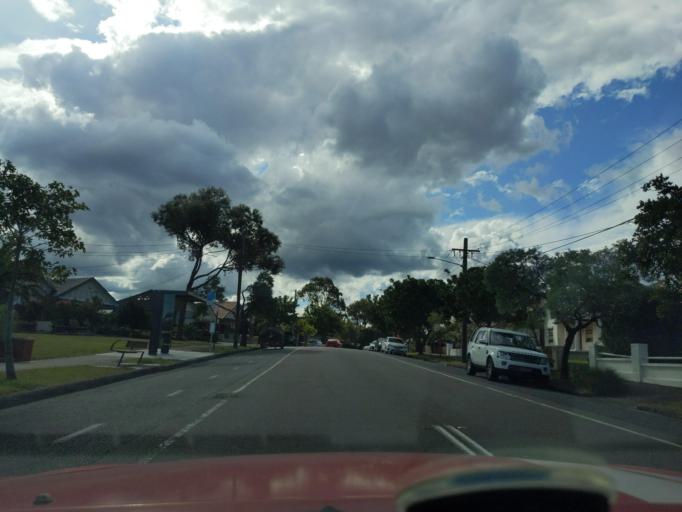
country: AU
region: New South Wales
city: Alexandria
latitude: -33.9205
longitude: 151.2072
